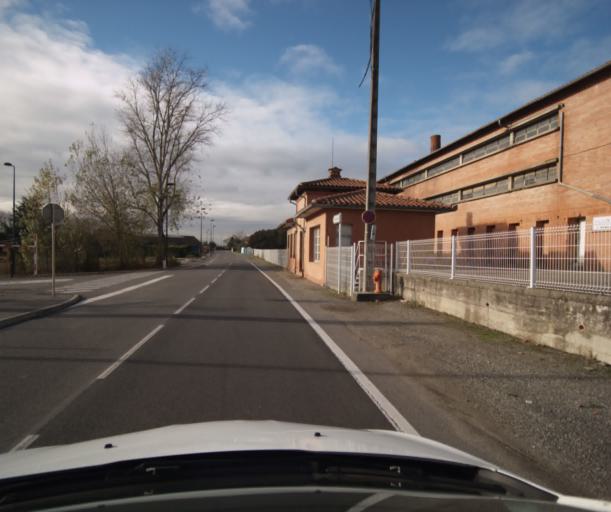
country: FR
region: Midi-Pyrenees
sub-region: Departement de la Haute-Garonne
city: Bruguieres
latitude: 43.7327
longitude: 1.4052
